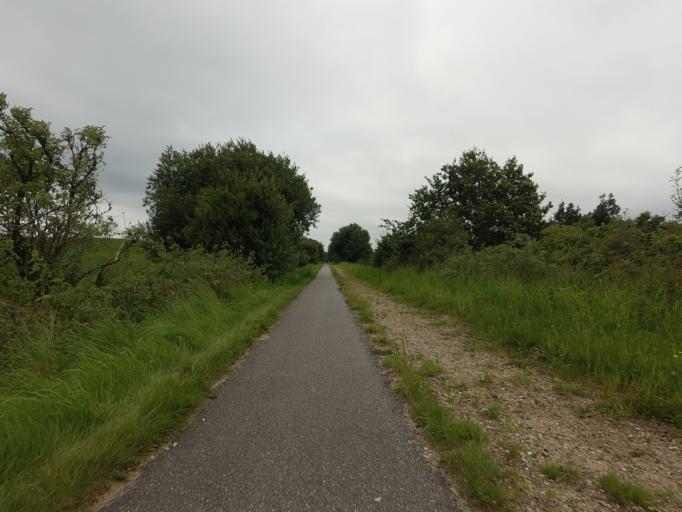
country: DK
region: Central Jutland
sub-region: Silkeborg Kommune
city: Virklund
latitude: 56.0917
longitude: 9.5326
